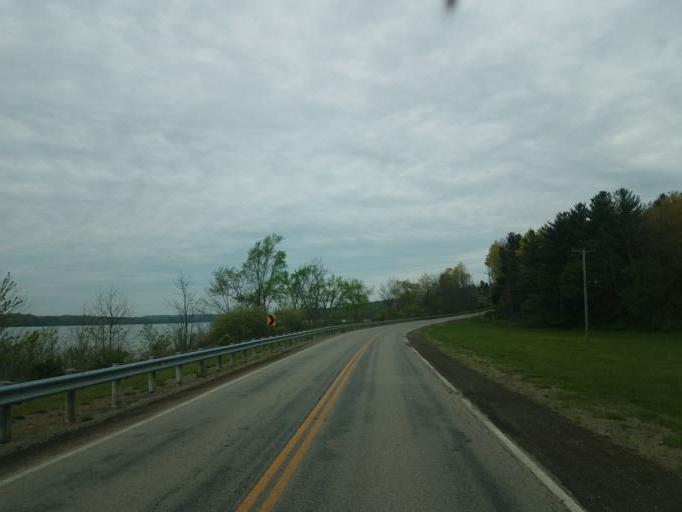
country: US
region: Ohio
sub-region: Richland County
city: Lexington
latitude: 40.7015
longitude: -82.6049
